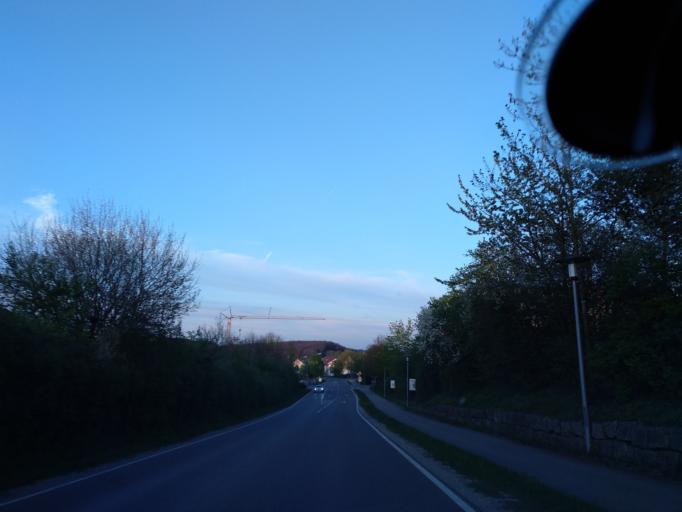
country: DE
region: Baden-Wuerttemberg
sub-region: Regierungsbezirk Stuttgart
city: Satteldorf
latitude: 49.1675
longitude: 10.0821
